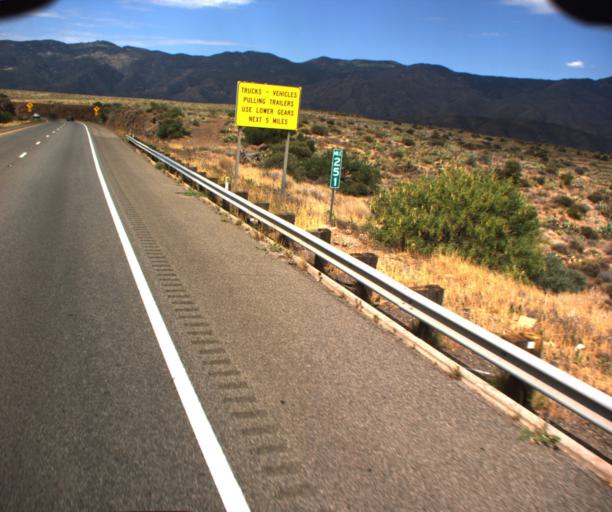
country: US
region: Arizona
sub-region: Yavapai County
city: Black Canyon City
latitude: 34.1722
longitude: -112.1395
